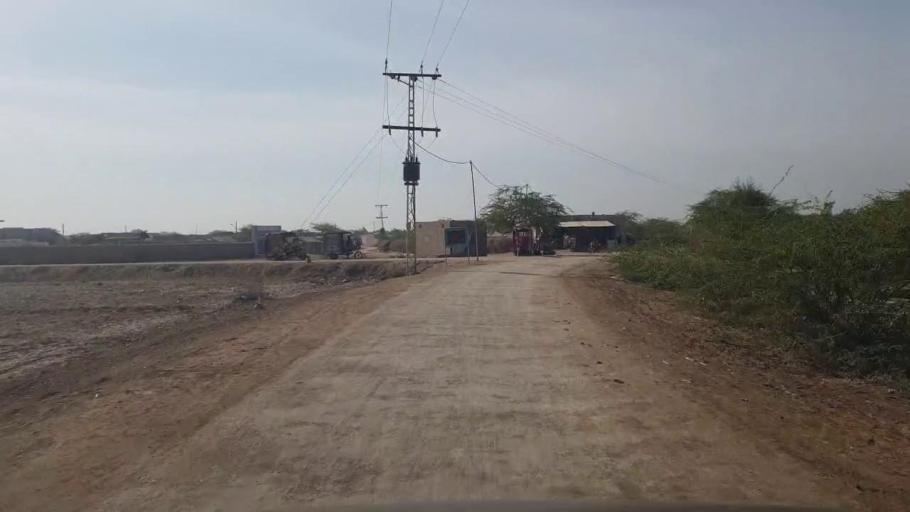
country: PK
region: Sindh
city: Umarkot
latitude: 25.3525
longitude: 69.6784
